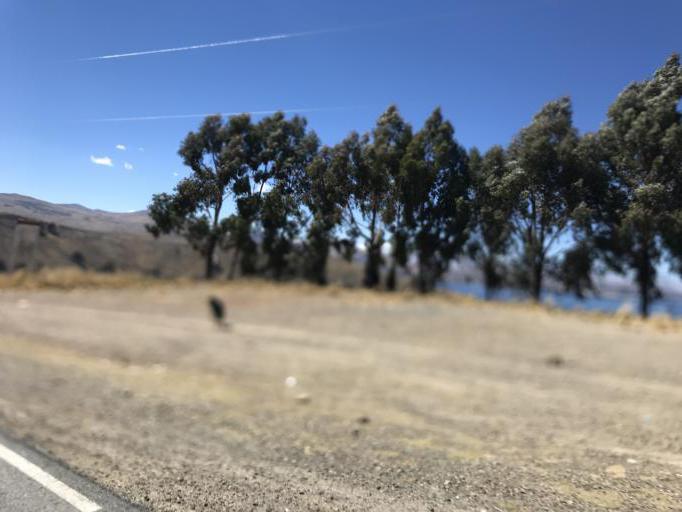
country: BO
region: La Paz
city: San Pablo
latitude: -16.2080
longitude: -68.8316
